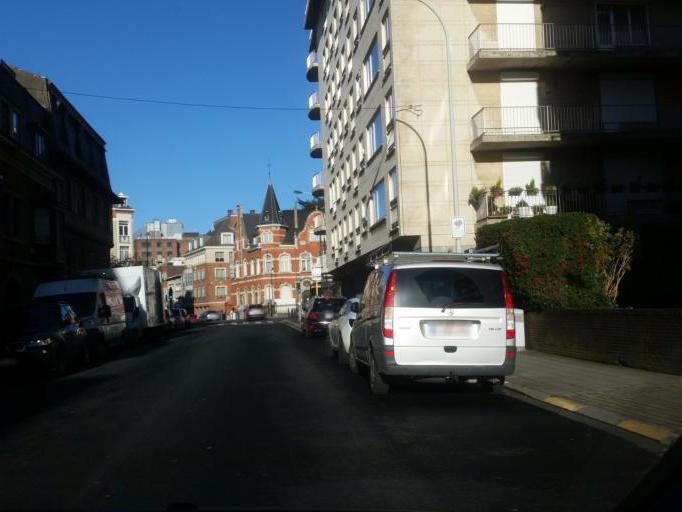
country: BE
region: Brussels Capital
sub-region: Bruxelles-Capitale
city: Brussels
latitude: 50.8108
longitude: 4.3576
